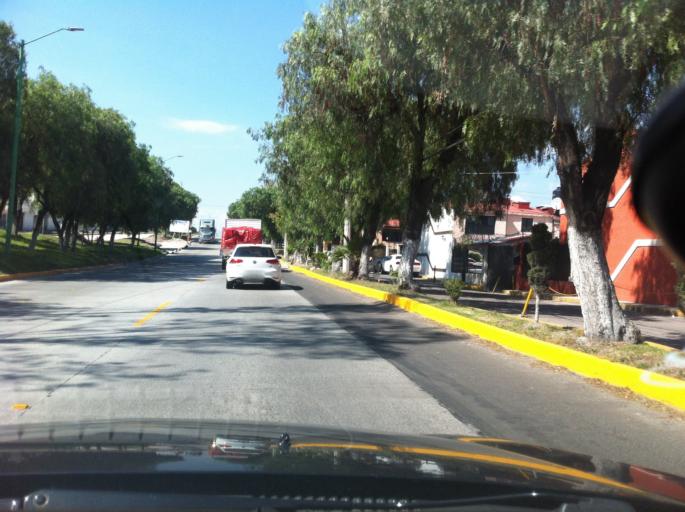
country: MX
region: Mexico
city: Cuautitlan Izcalli
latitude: 19.6439
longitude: -99.2018
